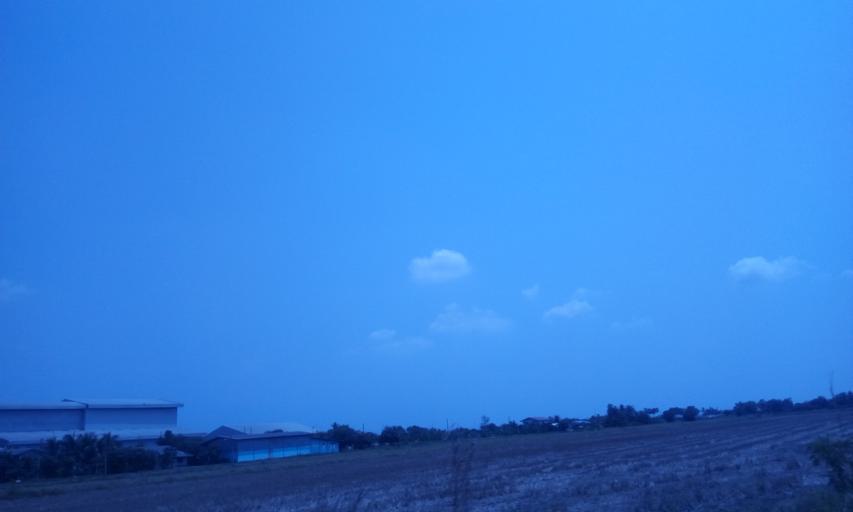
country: TH
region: Chachoengsao
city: Bang Nam Priao
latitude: 13.9497
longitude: 100.9746
